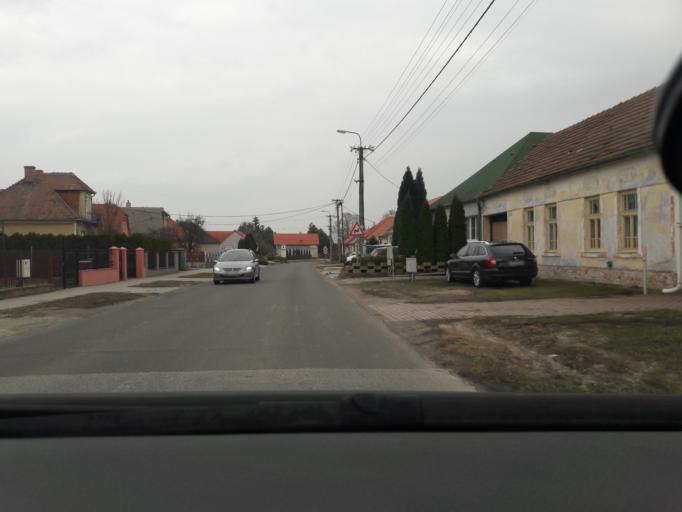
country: SK
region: Bratislavsky
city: Senec
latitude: 48.2977
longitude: 17.4529
